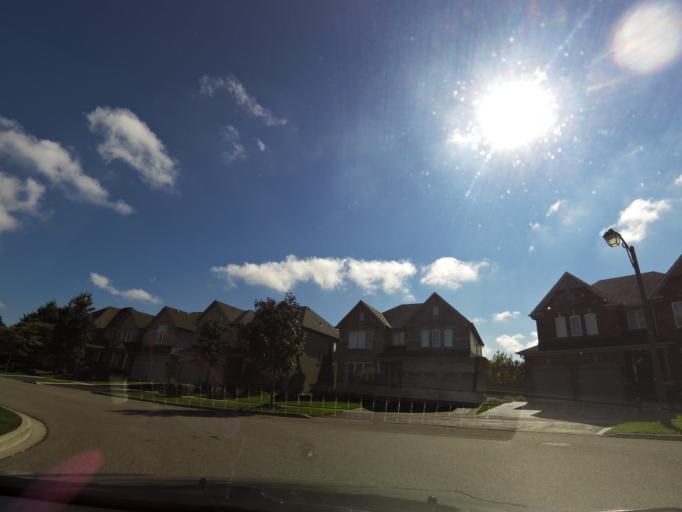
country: CA
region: Ontario
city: Burlington
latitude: 43.3970
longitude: -79.8133
